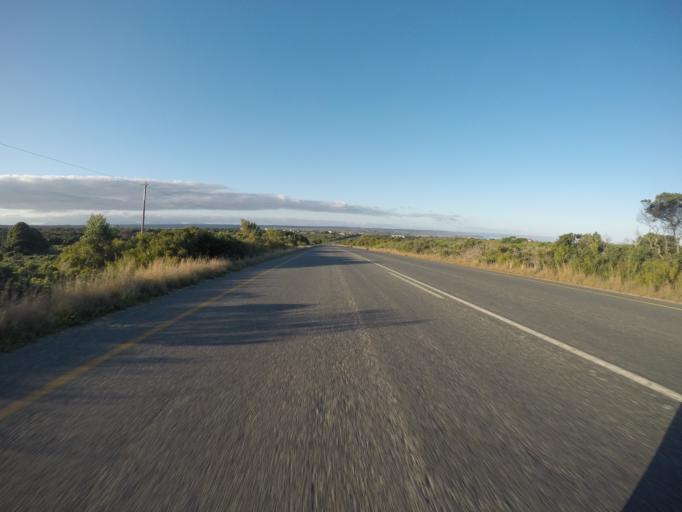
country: ZA
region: Western Cape
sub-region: Eden District Municipality
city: Riversdale
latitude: -34.3917
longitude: 21.3958
